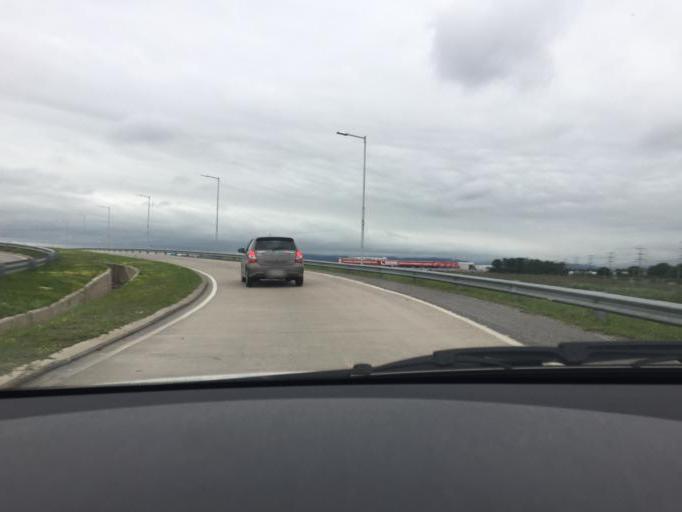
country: AR
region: Cordoba
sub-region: Departamento de Capital
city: Cordoba
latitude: -31.3529
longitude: -64.2035
